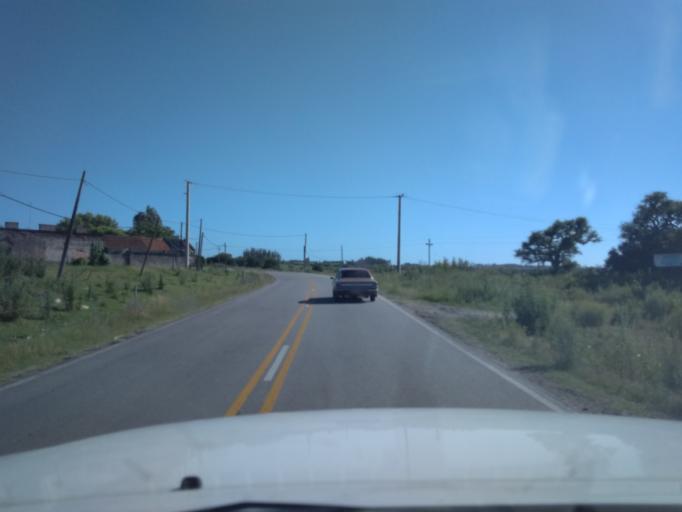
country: UY
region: Canelones
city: San Ramon
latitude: -34.3203
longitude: -55.9602
